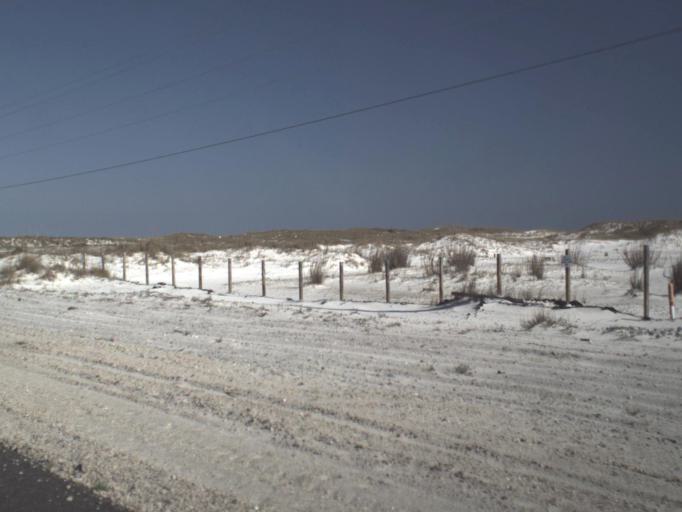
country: US
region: Florida
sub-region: Okaloosa County
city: Fort Walton Beach
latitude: 30.3953
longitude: -86.5799
